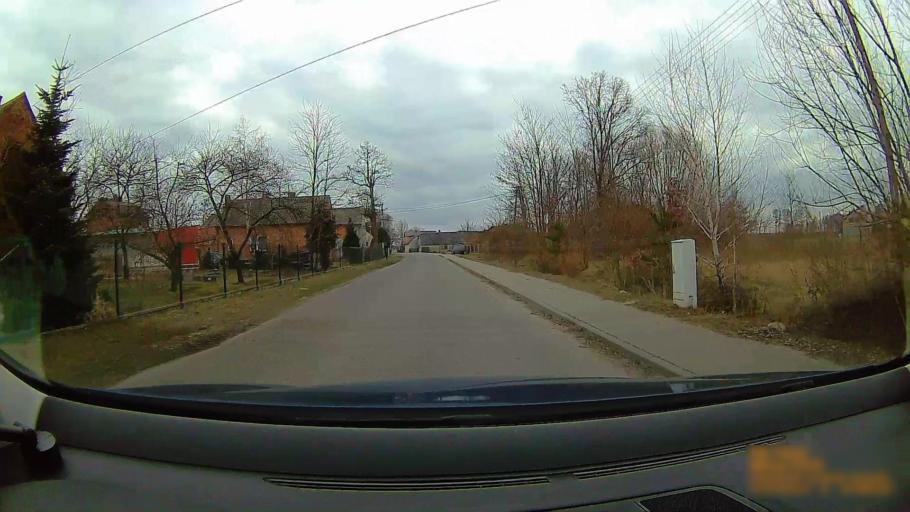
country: PL
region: Greater Poland Voivodeship
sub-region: Powiat koninski
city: Rychwal
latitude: 52.0790
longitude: 18.1361
